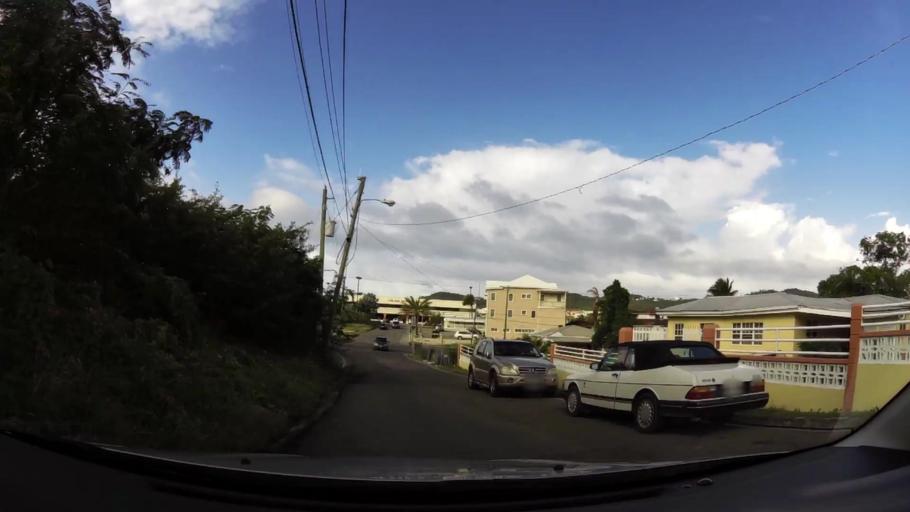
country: AG
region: Saint John
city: Saint John's
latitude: 17.1284
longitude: -61.8353
